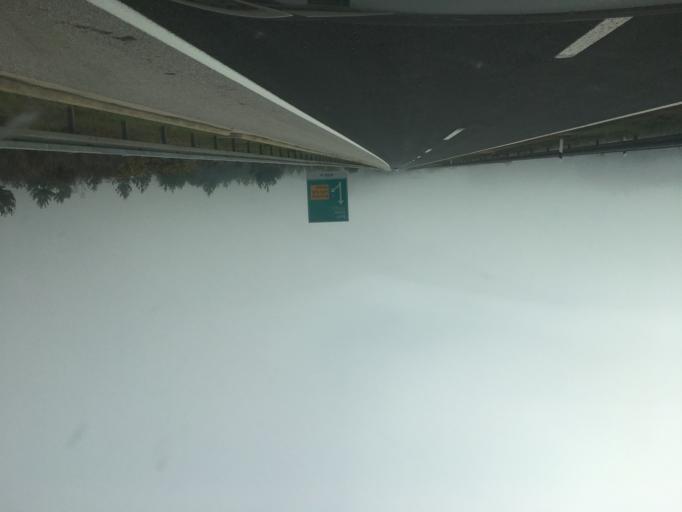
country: HR
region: Licko-Senjska
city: Gospic
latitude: 44.5879
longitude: 15.4335
